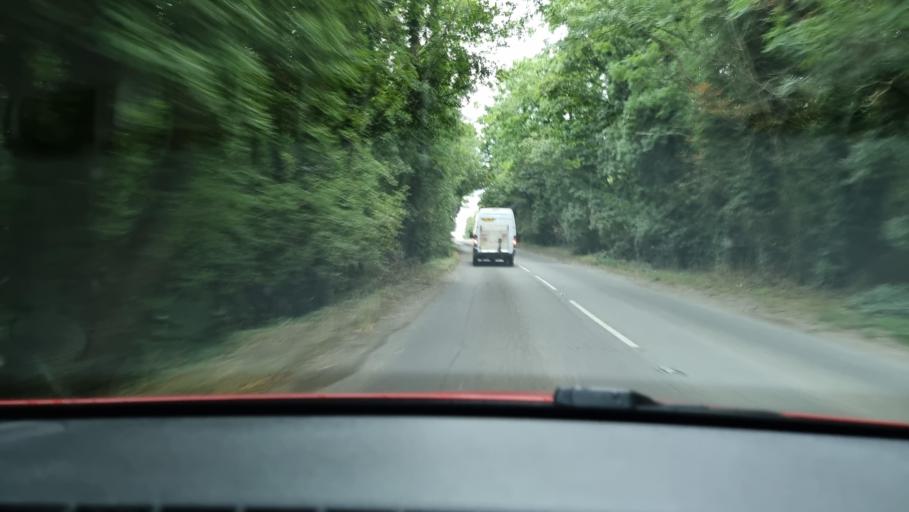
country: GB
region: England
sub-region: Buckinghamshire
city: Ivinghoe
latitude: 51.8209
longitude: -0.6319
